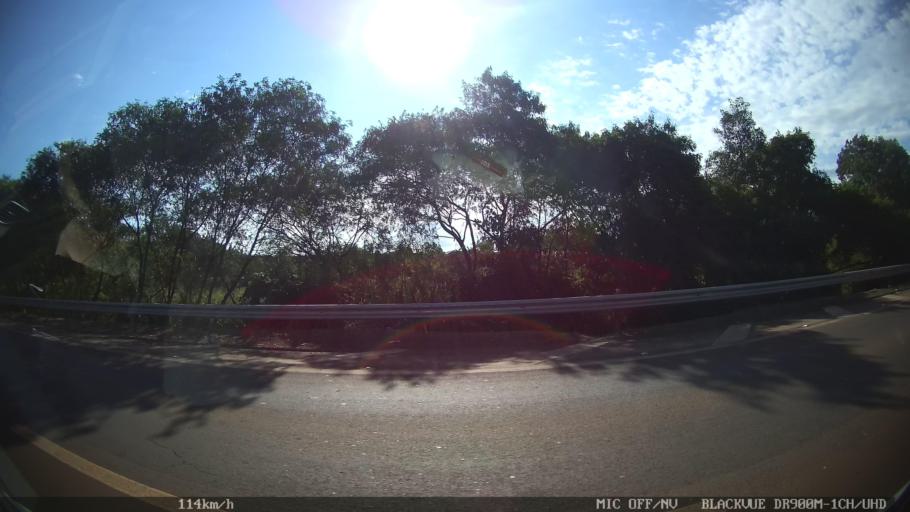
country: BR
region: Sao Paulo
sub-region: Iracemapolis
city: Iracemapolis
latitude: -22.6611
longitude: -47.5283
